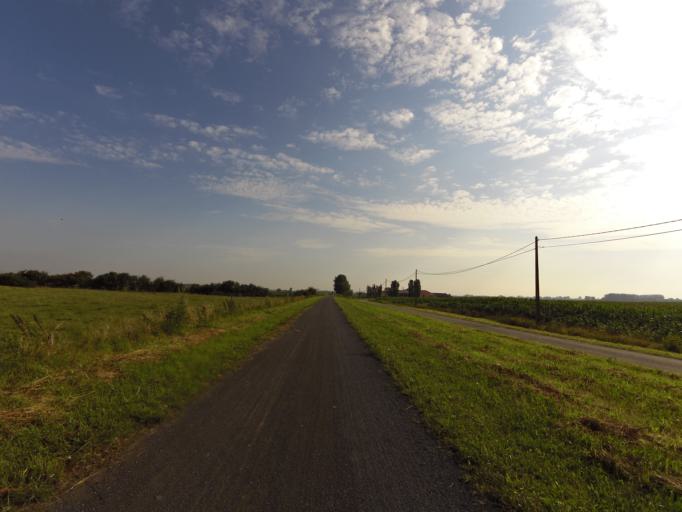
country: BE
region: Flanders
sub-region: Provincie West-Vlaanderen
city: Ostend
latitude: 51.1895
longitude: 2.9426
